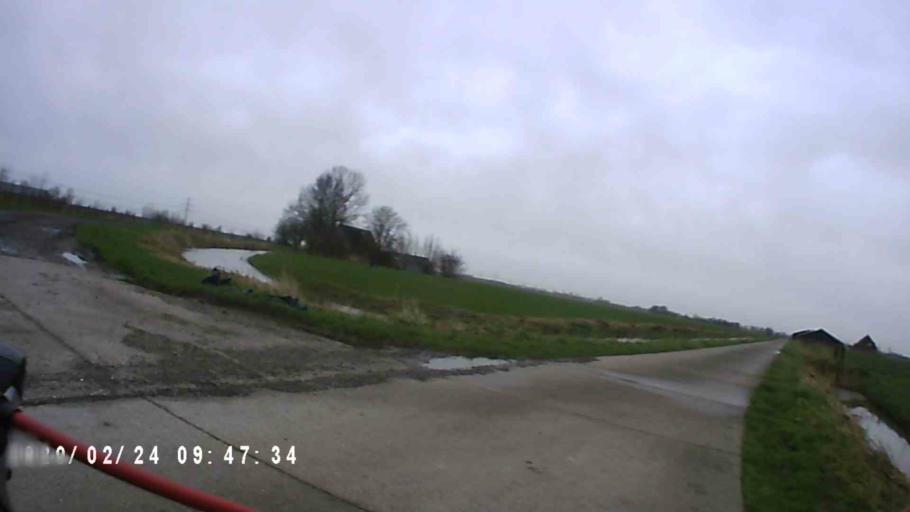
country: NL
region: Groningen
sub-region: Gemeente Winsum
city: Winsum
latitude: 53.2948
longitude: 6.5414
